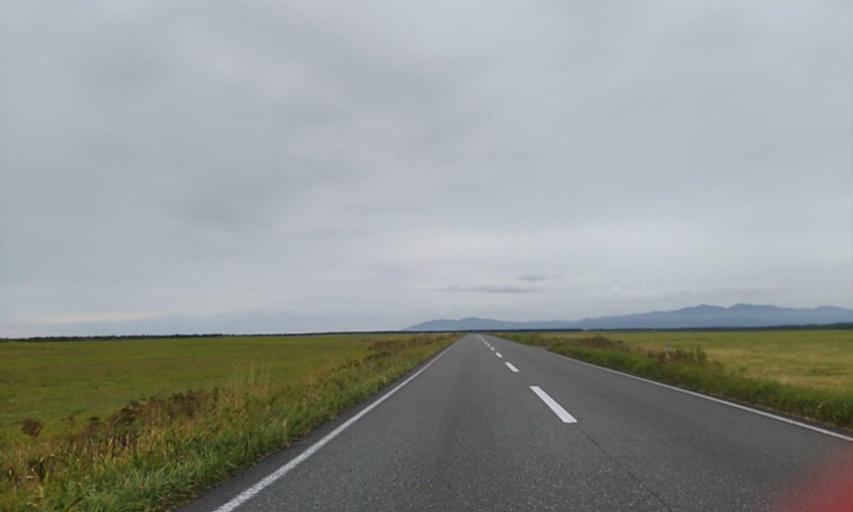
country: JP
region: Hokkaido
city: Makubetsu
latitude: 45.1857
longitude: 142.3171
